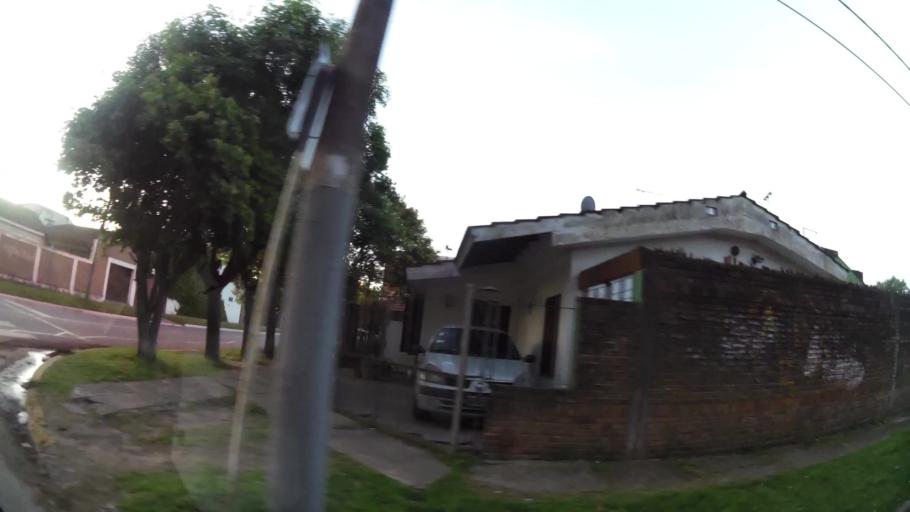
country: AR
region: Buenos Aires
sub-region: Partido de Quilmes
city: Quilmes
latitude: -34.7767
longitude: -58.2140
